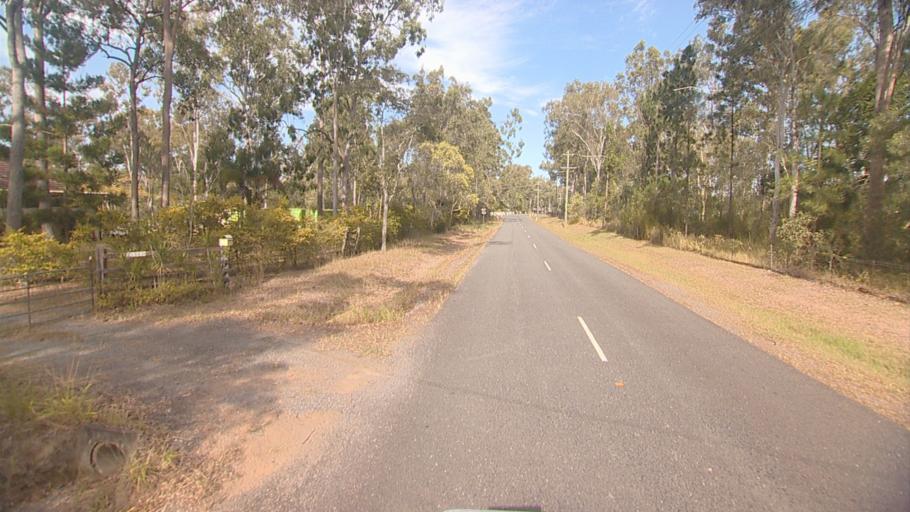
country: AU
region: Queensland
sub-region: Logan
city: North Maclean
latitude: -27.7456
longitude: 152.9736
